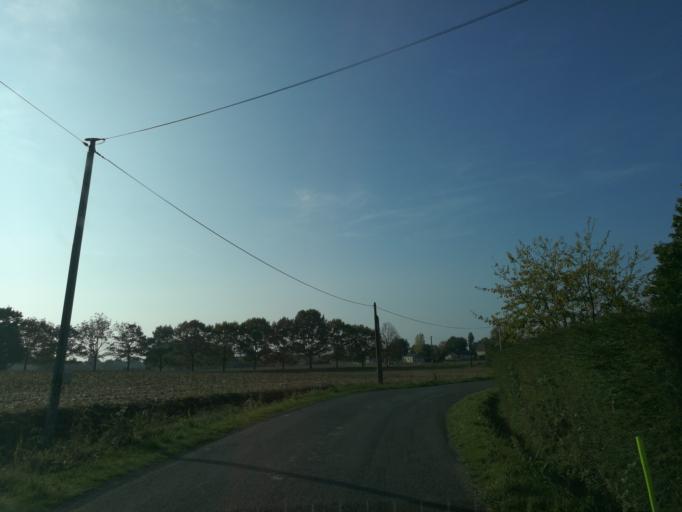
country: FR
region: Brittany
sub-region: Departement d'Ille-et-Vilaine
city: Breteil
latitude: 48.1544
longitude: -1.9161
